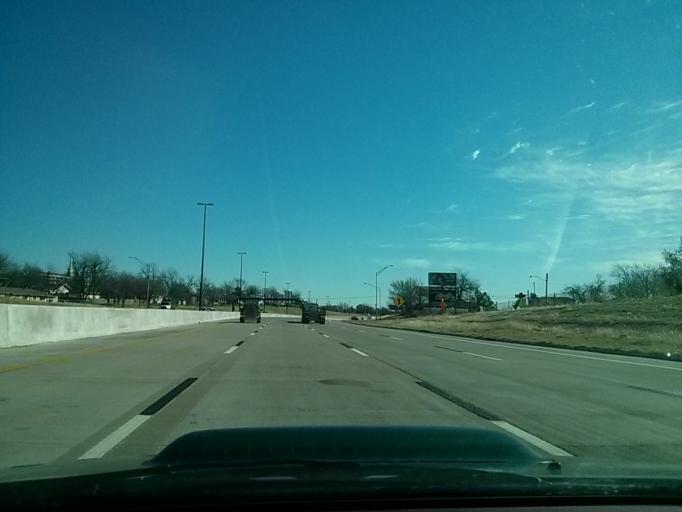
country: US
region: Oklahoma
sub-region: Tulsa County
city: Tulsa
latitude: 36.1593
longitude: -95.9644
